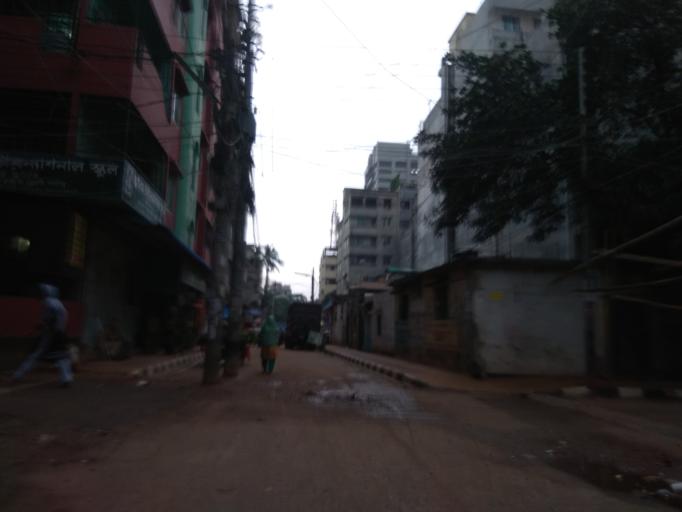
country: BD
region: Dhaka
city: Tungi
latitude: 23.8234
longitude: 90.3752
